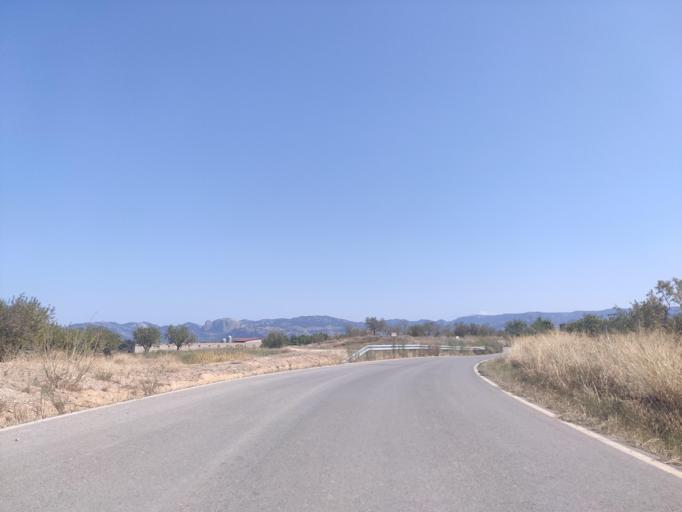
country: ES
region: Aragon
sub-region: Provincia de Teruel
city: Lledo
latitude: 40.9261
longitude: 0.2199
